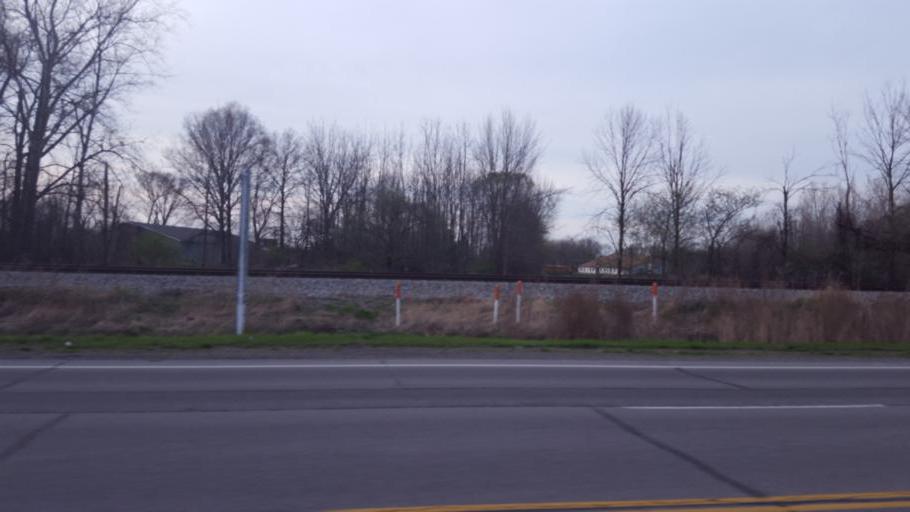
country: US
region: Ohio
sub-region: Lorain County
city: Lorain
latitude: 41.4498
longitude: -82.2126
